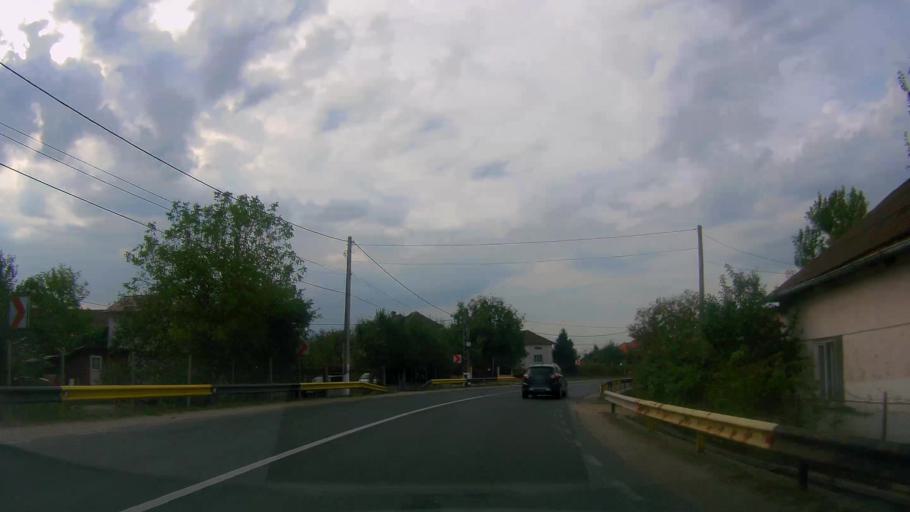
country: RO
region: Satu Mare
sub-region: Oras Ardud
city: Ardud
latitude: 47.5857
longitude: 22.8856
